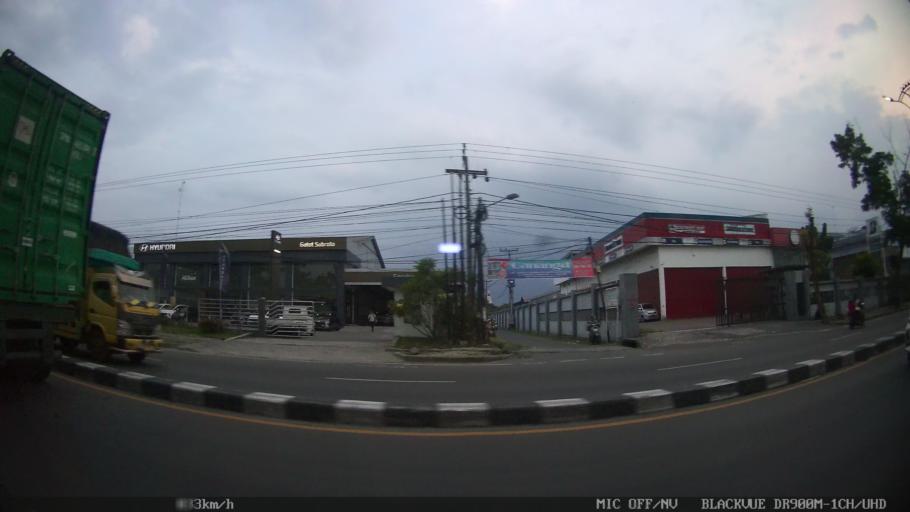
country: ID
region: North Sumatra
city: Sunggal
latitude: 3.5937
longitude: 98.6197
